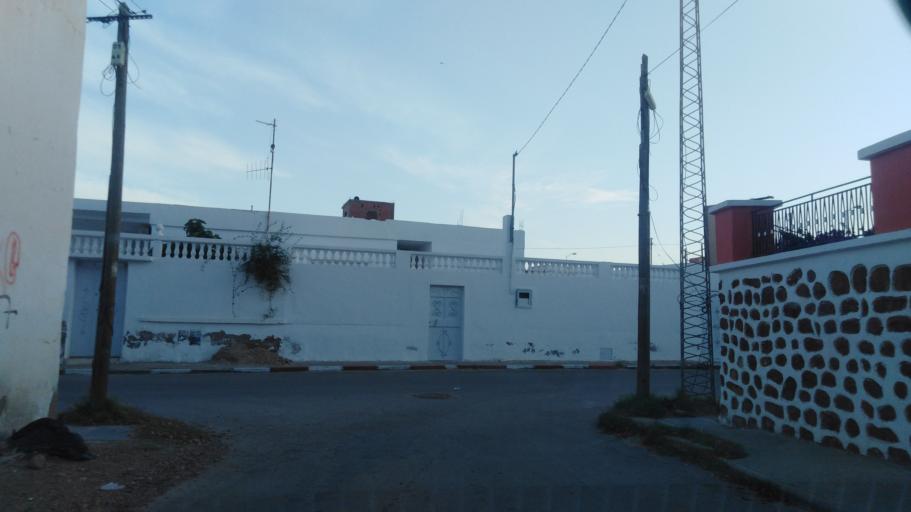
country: TN
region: Tataouine
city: Tataouine
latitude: 32.9386
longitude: 10.4526
